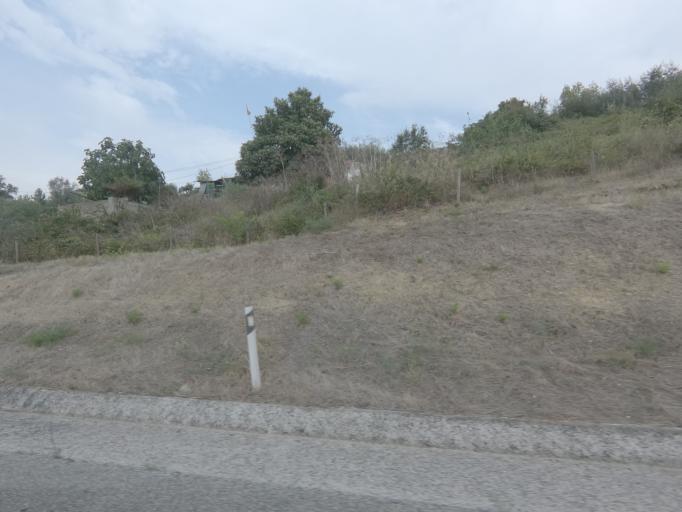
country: PT
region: Coimbra
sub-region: Coimbra
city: Coimbra
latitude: 40.2116
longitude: -8.4462
